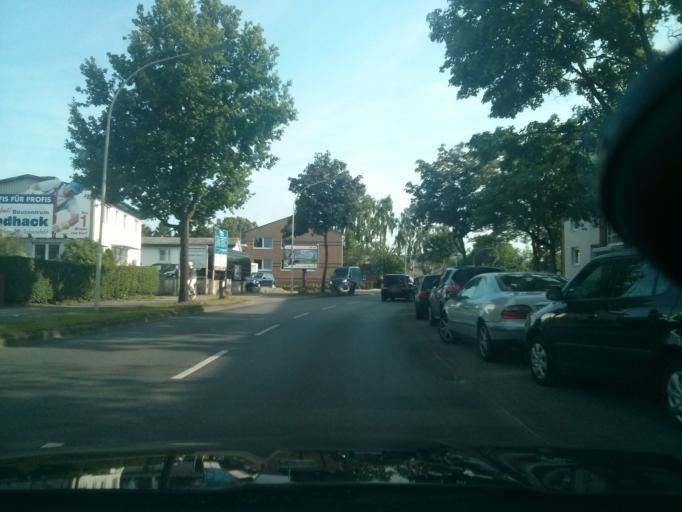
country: DE
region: Schleswig-Holstein
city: Halstenbek
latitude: 53.5989
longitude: 9.8381
